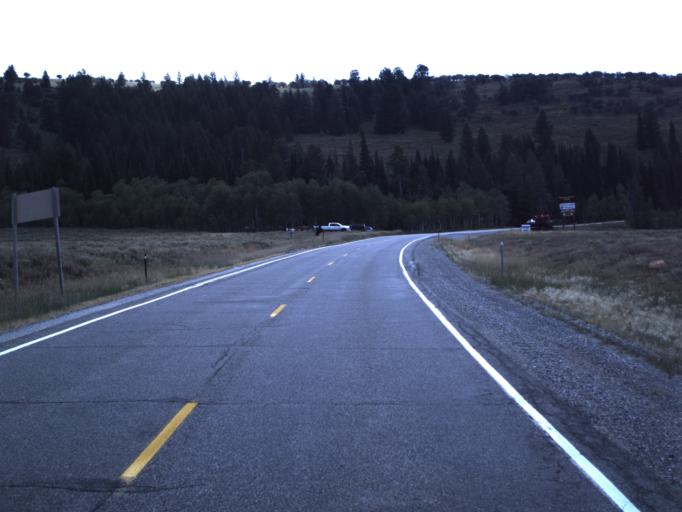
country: US
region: Idaho
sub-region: Bear Lake County
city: Paris
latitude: 41.9653
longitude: -111.5241
